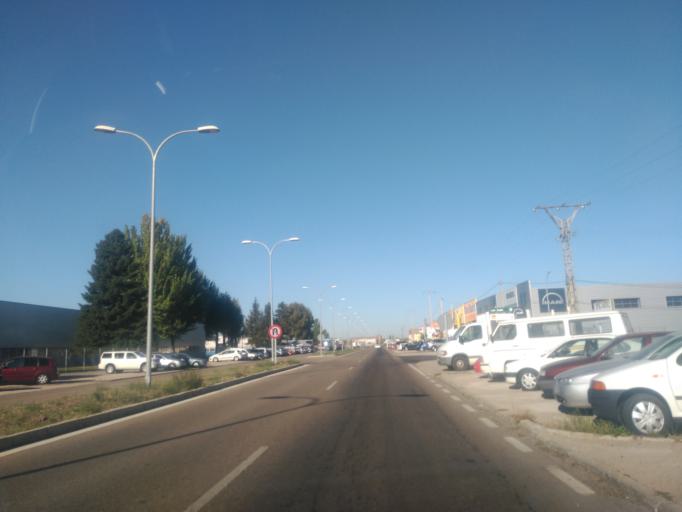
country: ES
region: Castille and Leon
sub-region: Provincia de Burgos
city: Aranda de Duero
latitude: 41.6653
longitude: -3.7102
